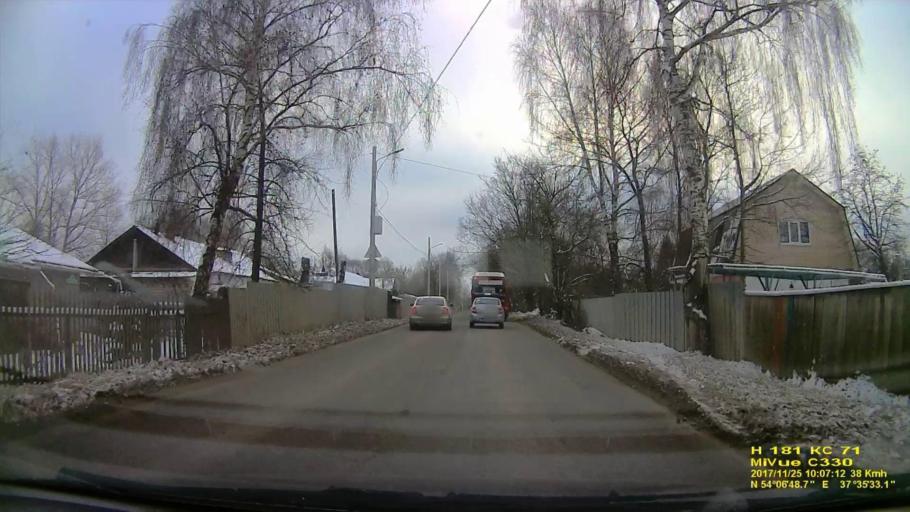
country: RU
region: Tula
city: Skuratovskiy
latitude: 54.1136
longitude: 37.5925
